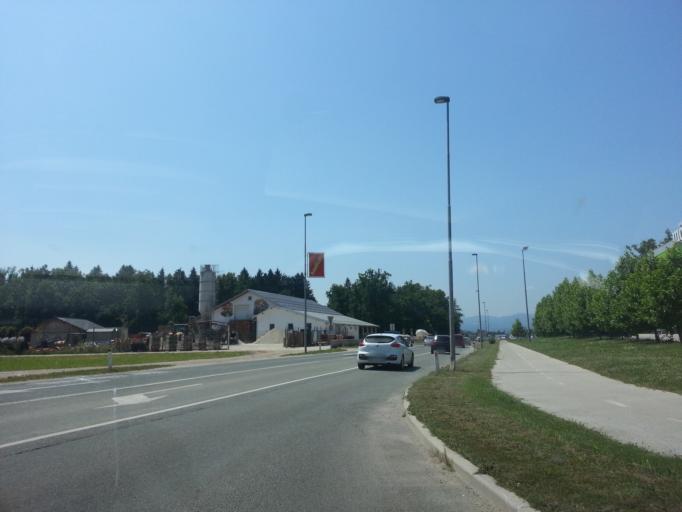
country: SI
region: Kranj
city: Kranj
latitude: 46.2368
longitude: 14.3753
